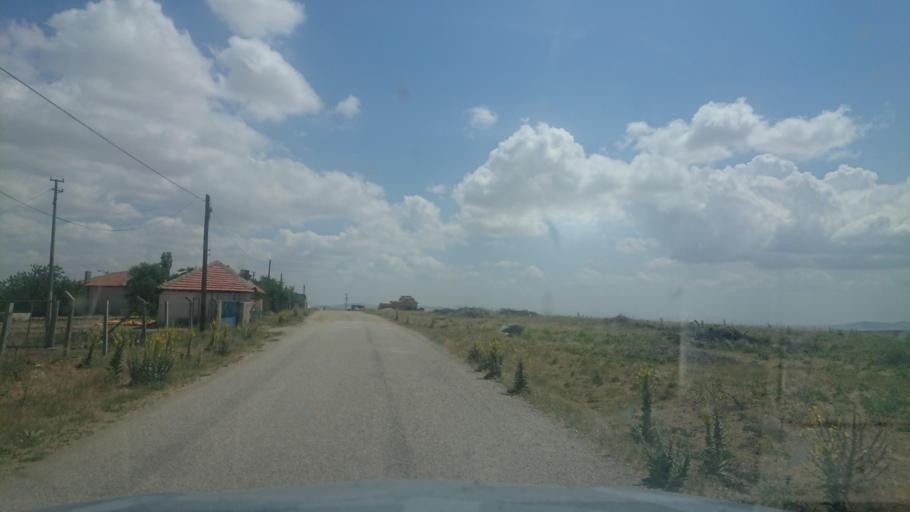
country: TR
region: Aksaray
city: Agacoren
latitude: 38.8787
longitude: 33.9520
